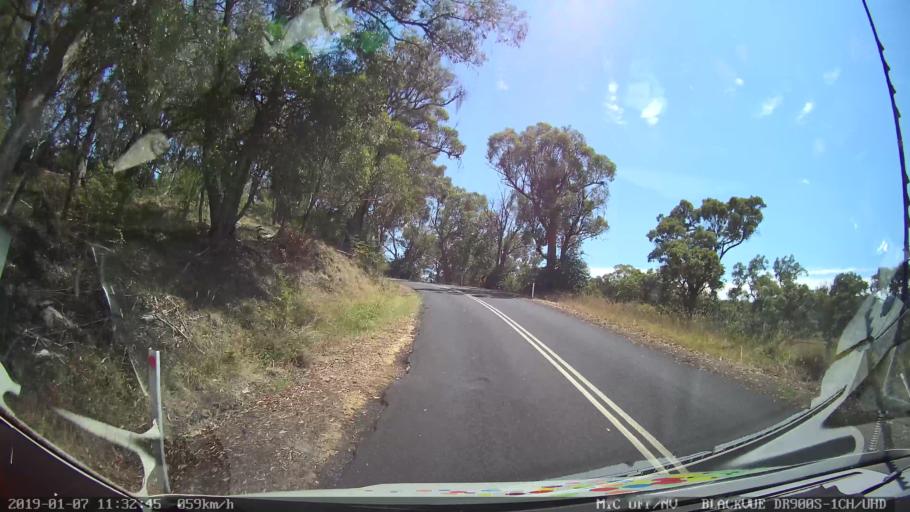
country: AU
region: New South Wales
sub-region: Armidale Dumaresq
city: Armidale
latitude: -30.4063
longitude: 151.5602
